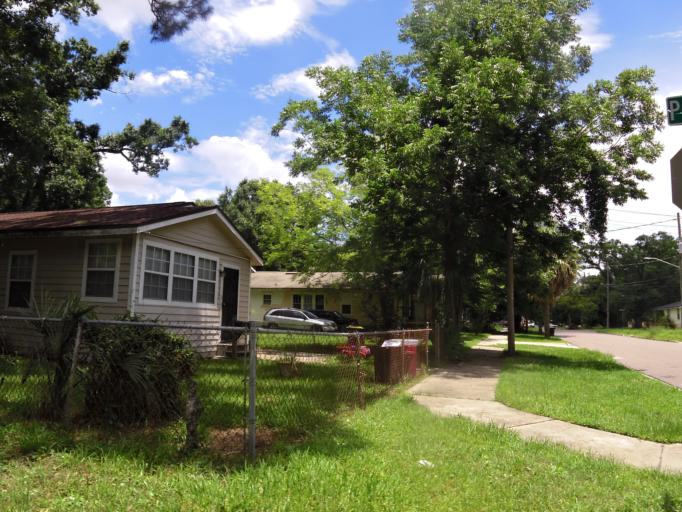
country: US
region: Florida
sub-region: Duval County
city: Jacksonville
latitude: 30.3465
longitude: -81.6841
